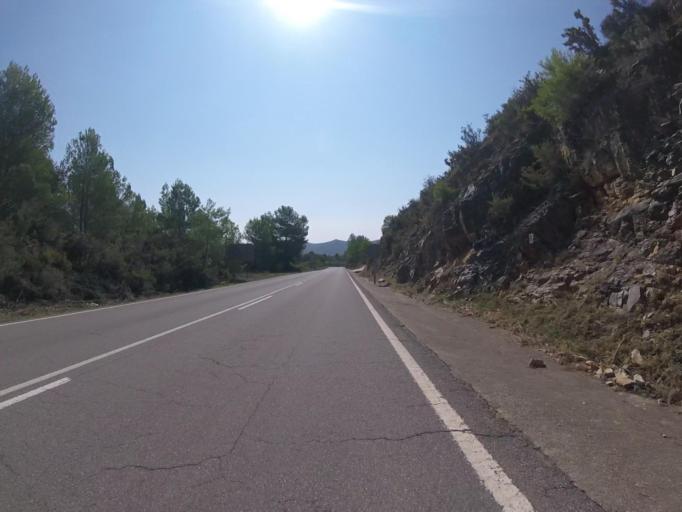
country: ES
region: Valencia
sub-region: Provincia de Castello
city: Adzaneta
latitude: 40.2363
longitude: -0.1829
